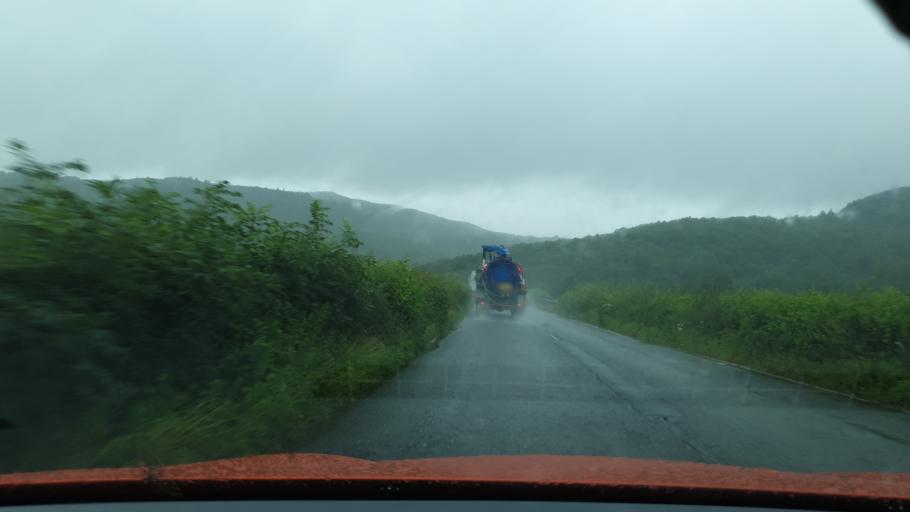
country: GB
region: England
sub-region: Cumbria
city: Millom
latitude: 54.2816
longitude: -3.2228
